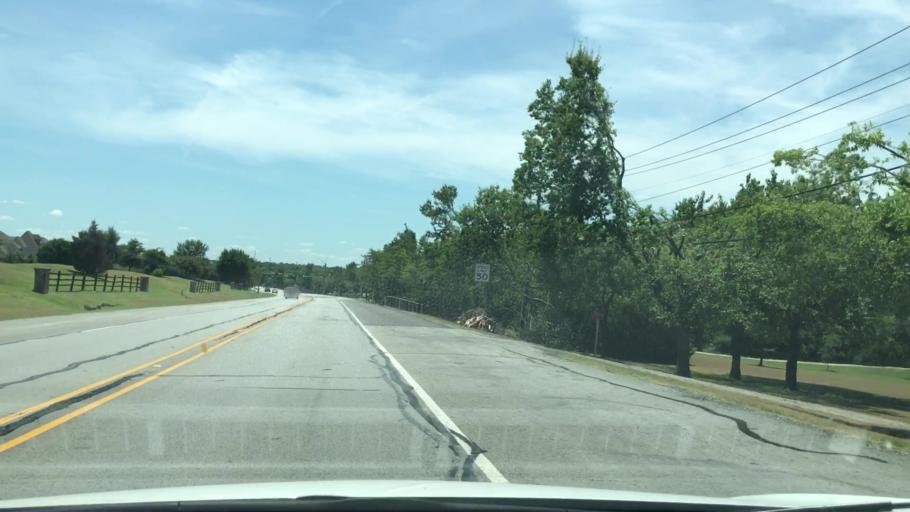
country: US
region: Texas
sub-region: Rockwall County
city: Rockwall
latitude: 32.9603
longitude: -96.4648
